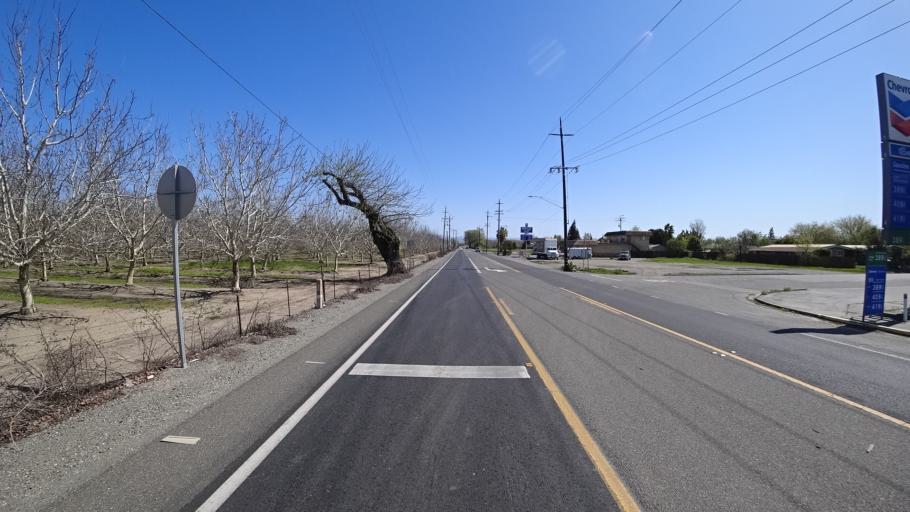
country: US
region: California
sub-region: Glenn County
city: Hamilton City
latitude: 39.7469
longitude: -122.0110
